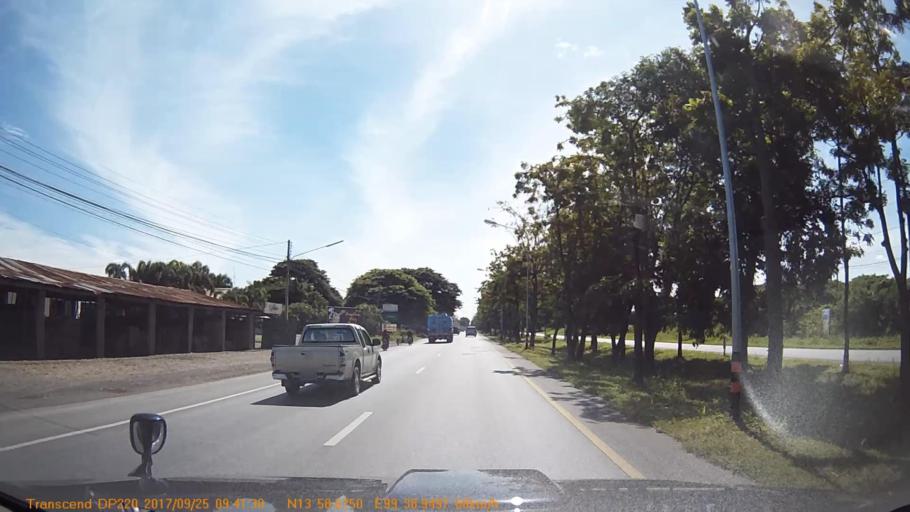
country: TH
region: Kanchanaburi
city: Tha Muang
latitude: 13.9779
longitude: 99.6496
